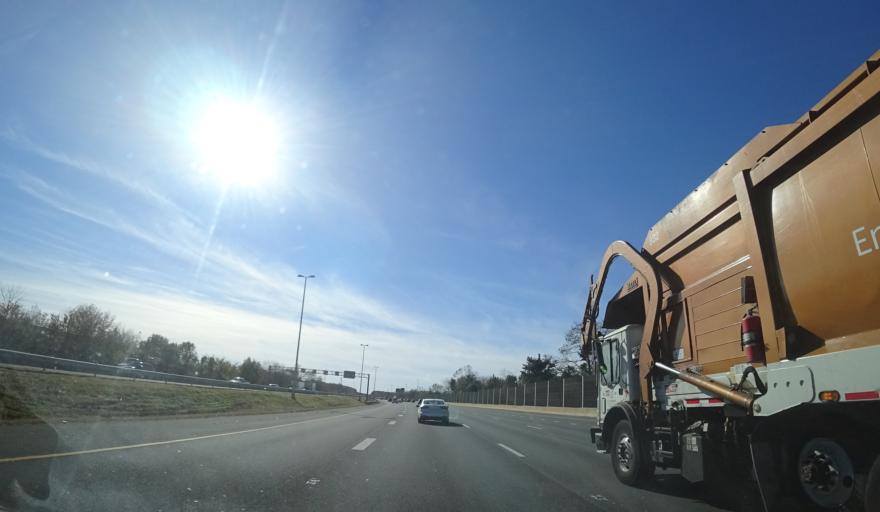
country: US
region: Virginia
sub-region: Fairfax County
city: Centreville
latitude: 38.8424
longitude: -77.4426
